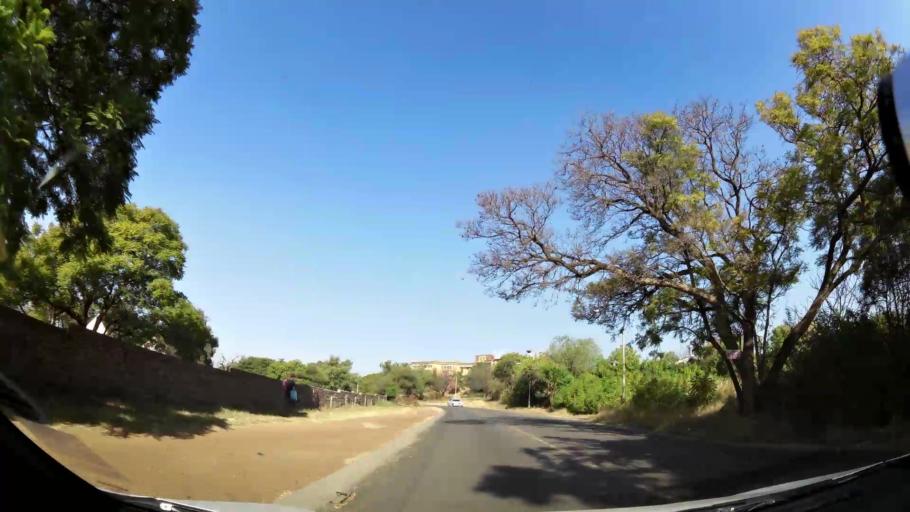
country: ZA
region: North-West
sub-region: Bojanala Platinum District Municipality
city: Rustenburg
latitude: -25.6760
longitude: 27.2445
